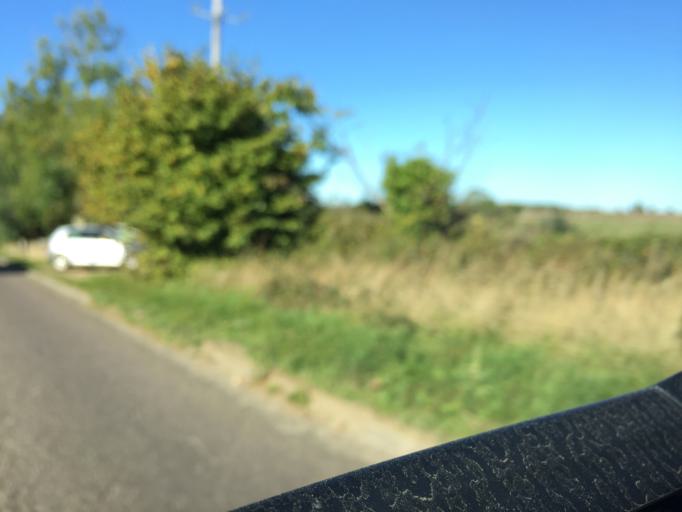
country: GB
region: England
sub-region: Wiltshire
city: Colerne
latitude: 51.4674
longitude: -2.2740
